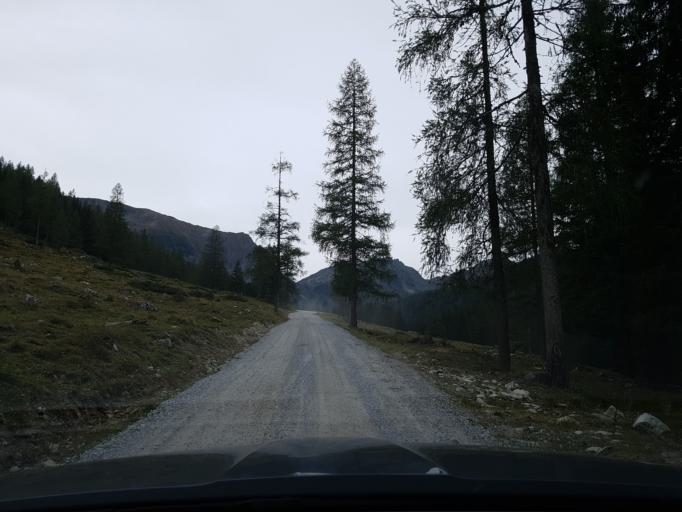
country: AT
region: Salzburg
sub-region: Politischer Bezirk Sankt Johann im Pongau
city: Forstau
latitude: 47.3064
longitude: 13.5826
